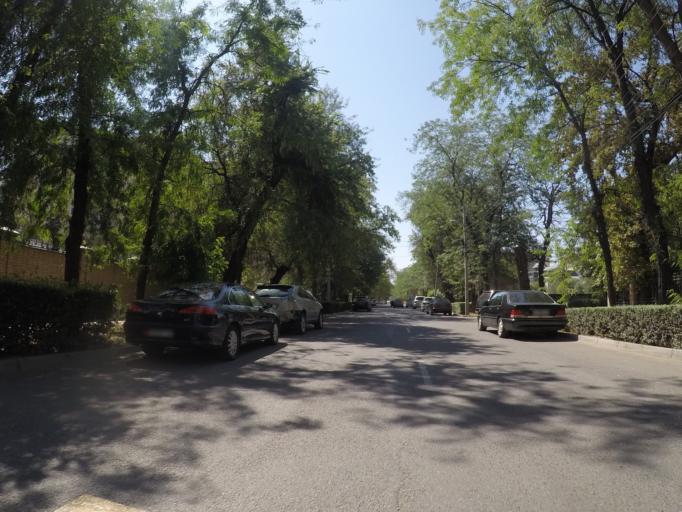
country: KG
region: Chuy
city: Bishkek
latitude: 42.8803
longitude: 74.5920
